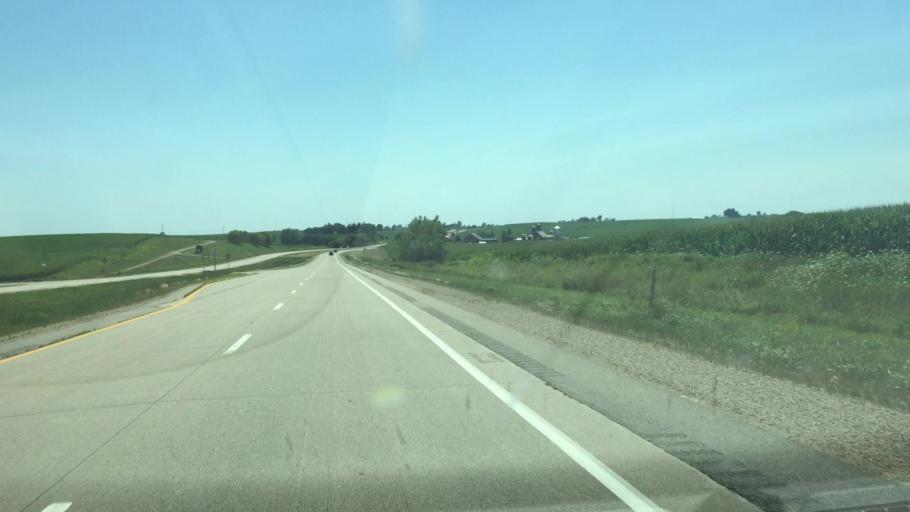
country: US
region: Iowa
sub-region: Dubuque County
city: Peosta
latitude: 42.3506
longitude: -90.8292
